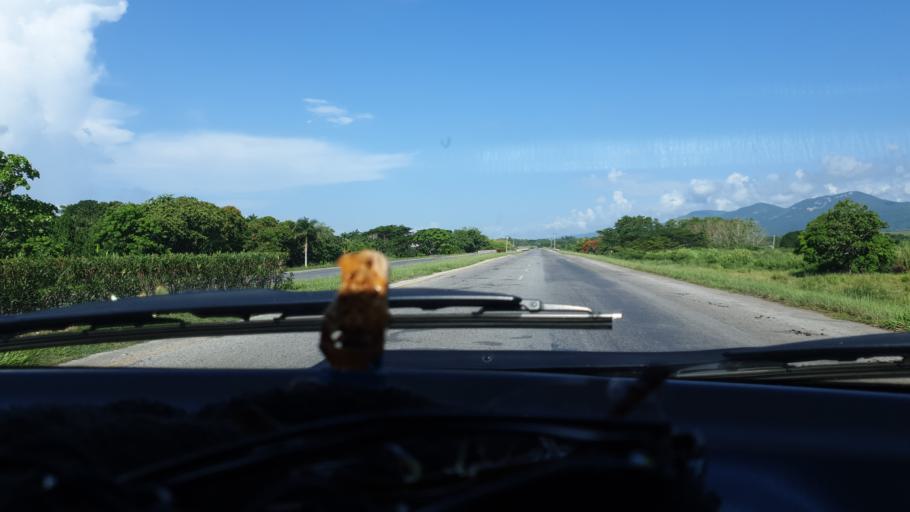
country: CU
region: Artemisa
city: San Cristobal
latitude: 22.7224
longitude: -83.0396
